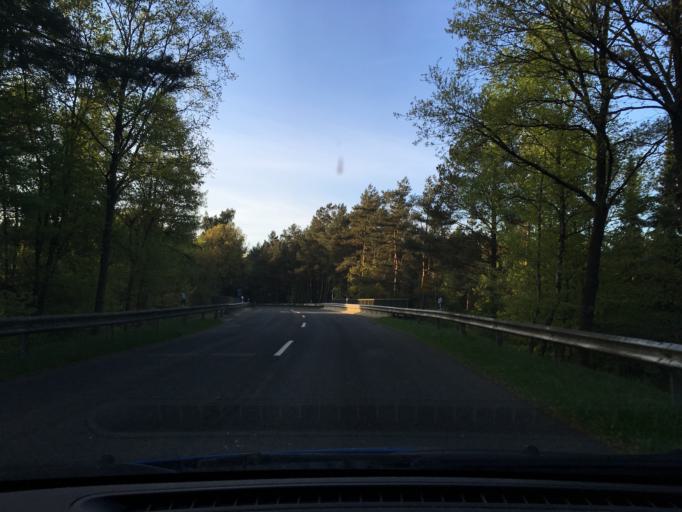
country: DE
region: Lower Saxony
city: Bispingen
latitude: 53.0001
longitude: 9.9997
